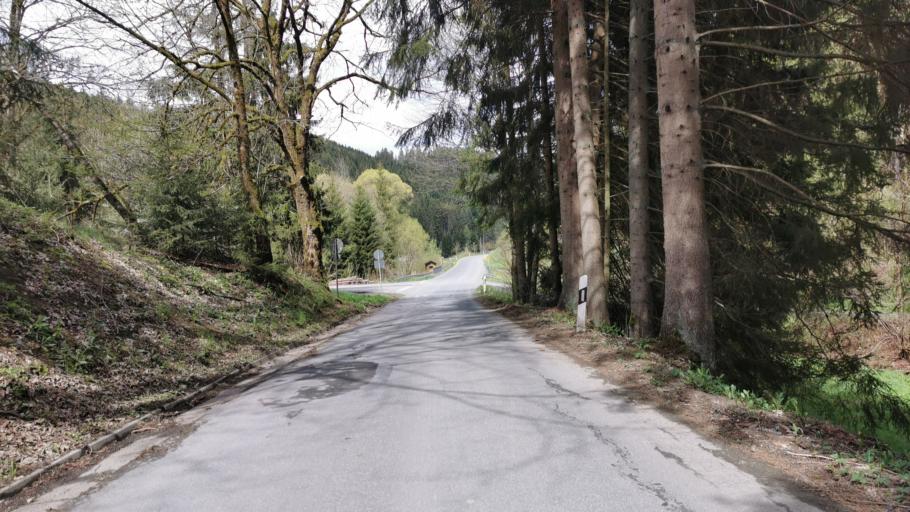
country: DE
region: Bavaria
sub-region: Upper Franconia
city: Ludwigsstadt
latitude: 50.4777
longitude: 11.3663
